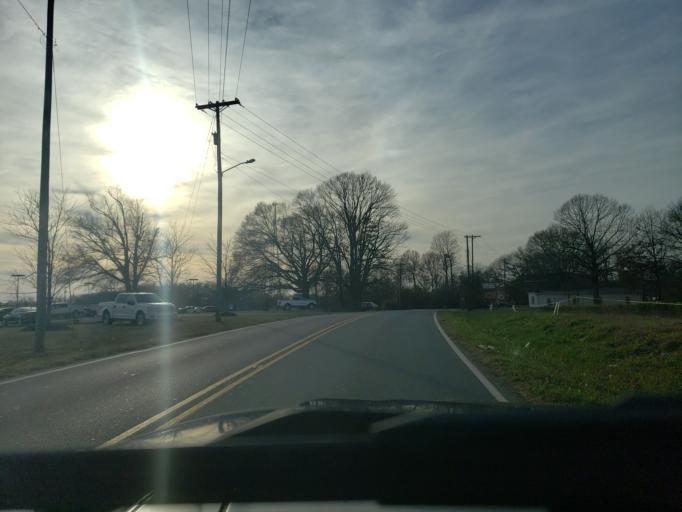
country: US
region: North Carolina
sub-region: Cleveland County
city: Shelby
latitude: 35.2745
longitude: -81.4984
